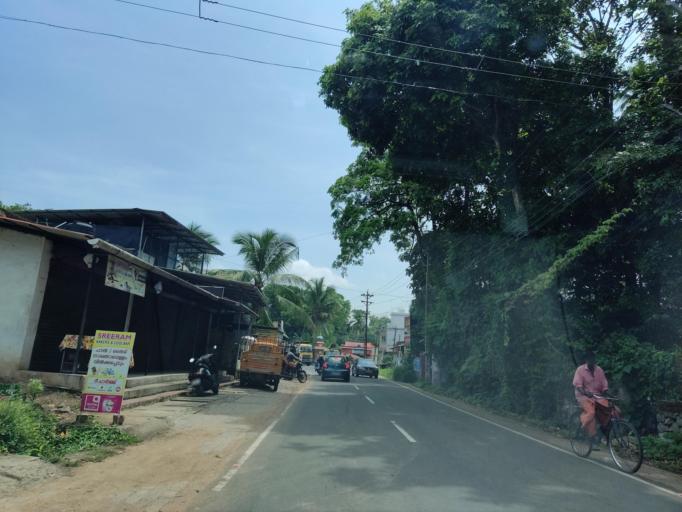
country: IN
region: Kerala
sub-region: Alappuzha
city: Chengannur
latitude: 9.3096
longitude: 76.5980
